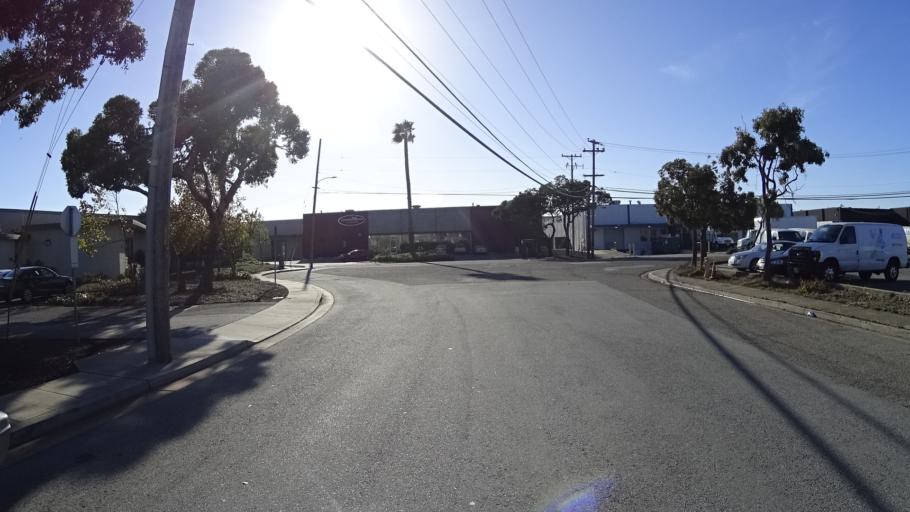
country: US
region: California
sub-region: San Mateo County
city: South San Francisco
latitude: 37.6442
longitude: -122.3983
